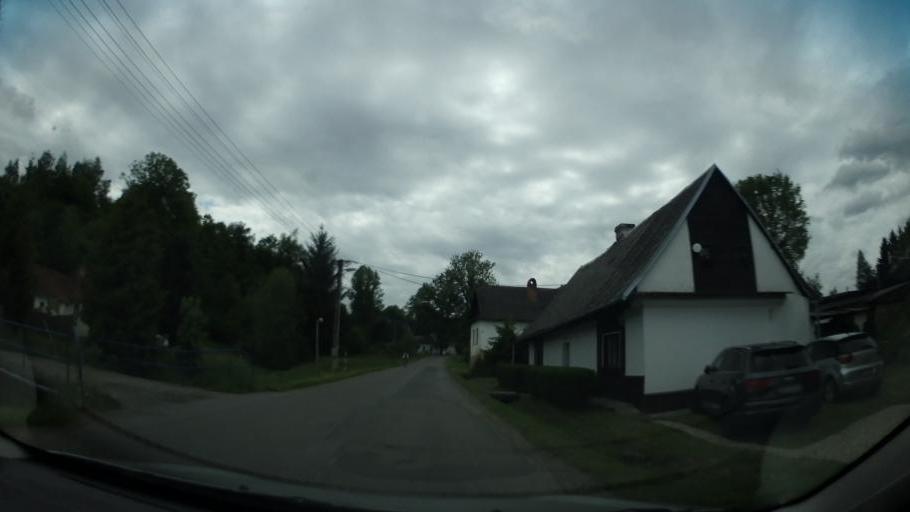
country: CZ
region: Pardubicky
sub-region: Okres Svitavy
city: Moravska Trebova
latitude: 49.8210
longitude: 16.7010
